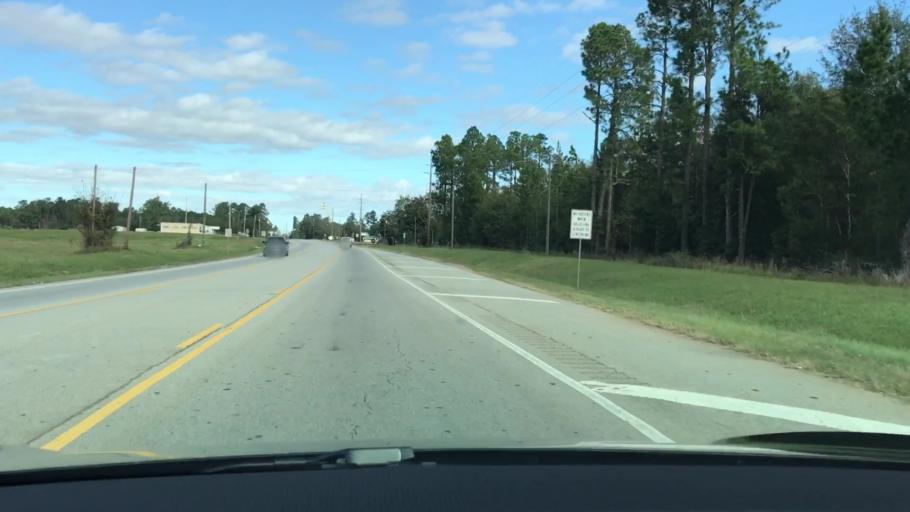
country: US
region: Georgia
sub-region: Jefferson County
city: Louisville
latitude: 33.0269
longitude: -82.4045
